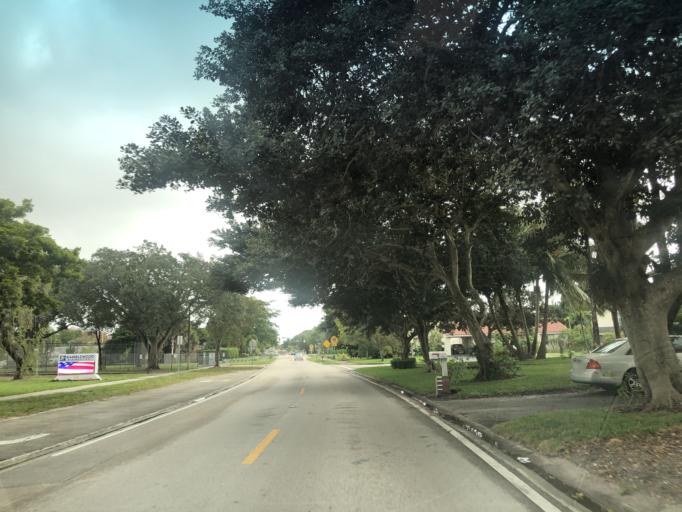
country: US
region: Florida
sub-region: Broward County
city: Tamarac
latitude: 26.2473
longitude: -80.2450
